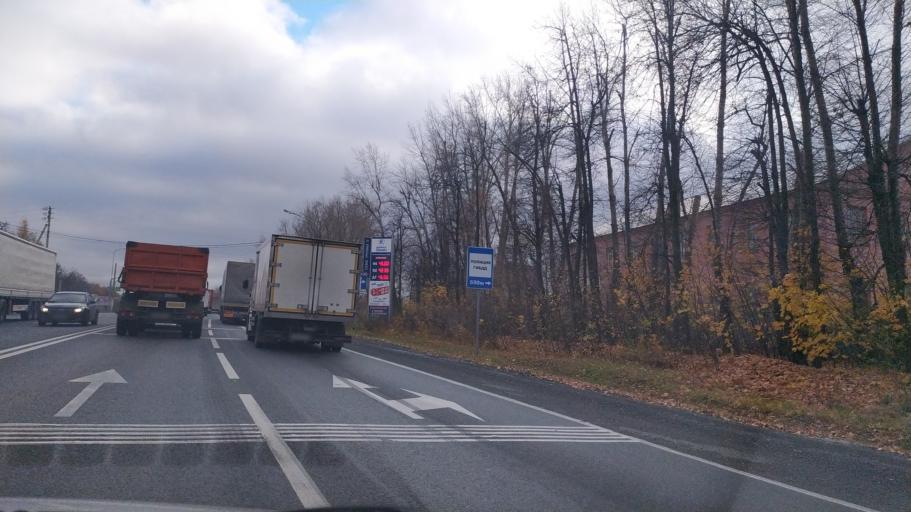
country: RU
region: Chuvashia
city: Kugesi
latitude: 56.0431
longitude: 47.2923
